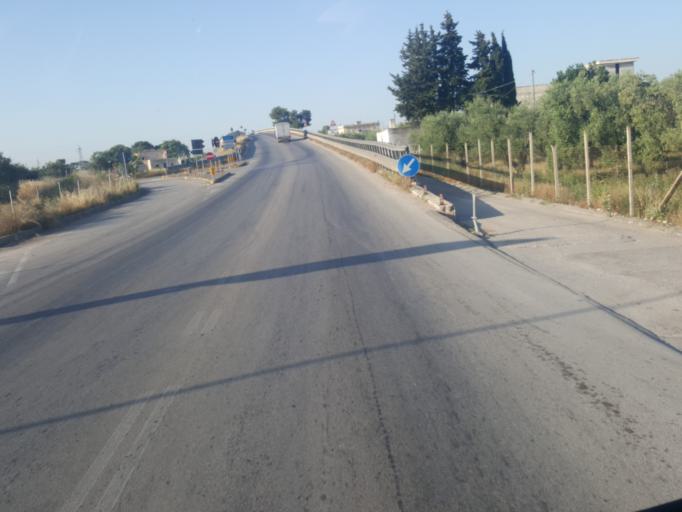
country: IT
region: Apulia
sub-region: Provincia di Foggia
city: Cerignola
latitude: 41.3192
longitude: 15.9001
